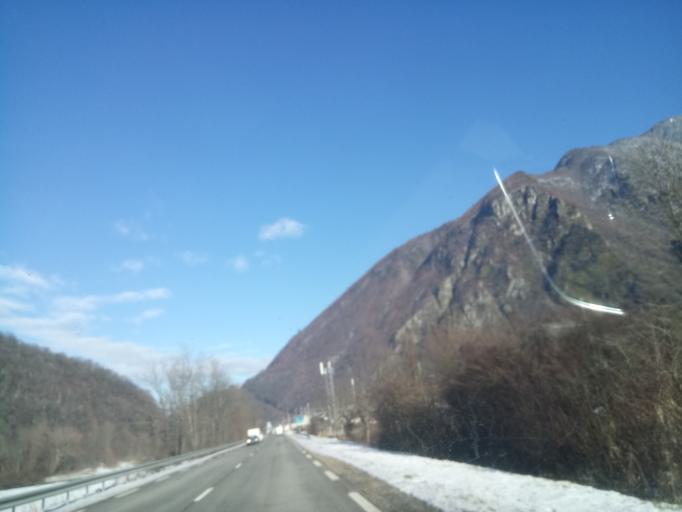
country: FR
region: Rhone-Alpes
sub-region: Departement de la Savoie
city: Saint-Remy-de-Maurienne
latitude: 45.4529
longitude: 6.2905
